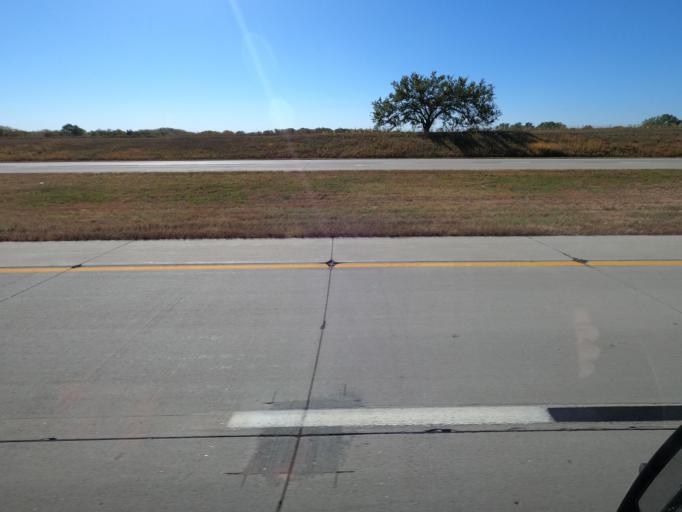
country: US
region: Kansas
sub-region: Geary County
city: Junction City
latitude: 39.0022
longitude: -96.9148
